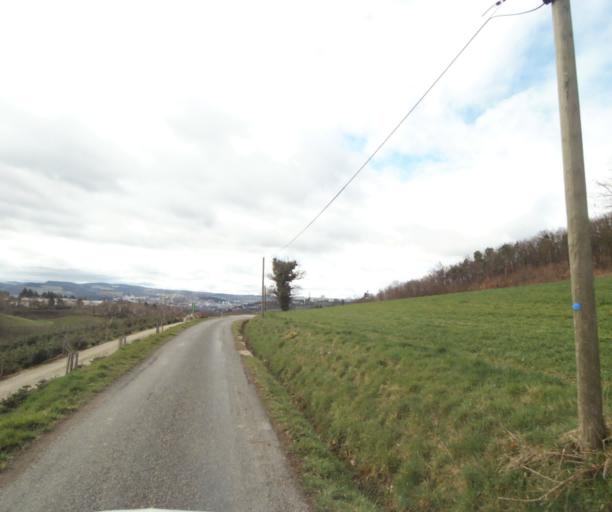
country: FR
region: Rhone-Alpes
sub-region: Departement de la Loire
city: La Talaudiere
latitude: 45.4903
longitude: 4.4160
